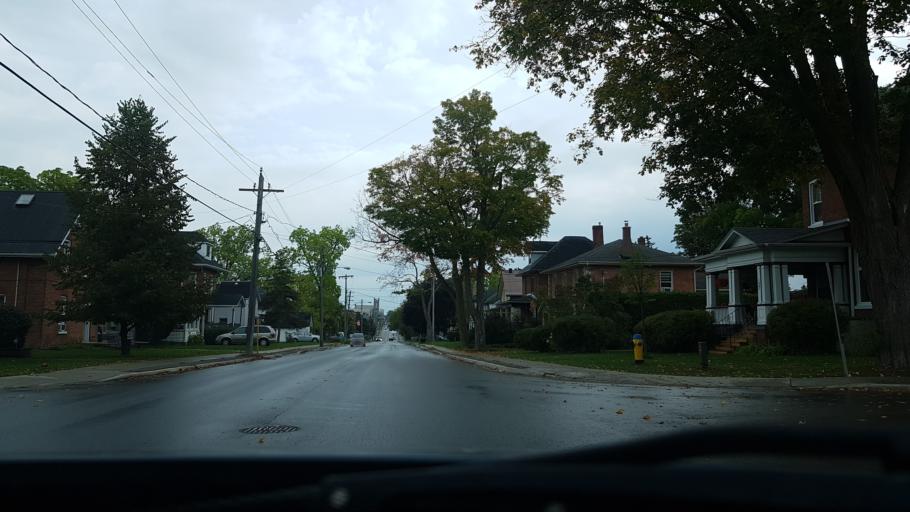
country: CA
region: Ontario
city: Omemee
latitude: 44.3621
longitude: -78.7404
